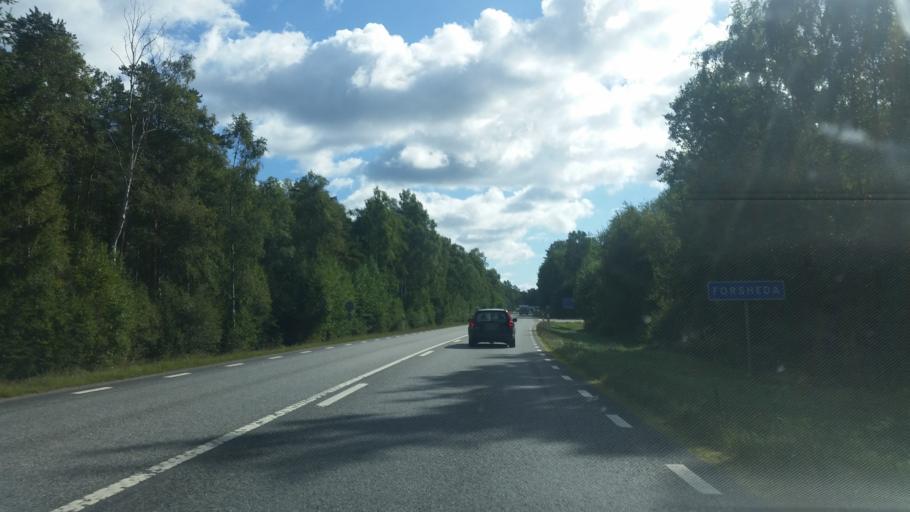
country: SE
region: Joenkoeping
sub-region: Varnamo Kommun
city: Forsheda
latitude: 57.1674
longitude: 13.8264
